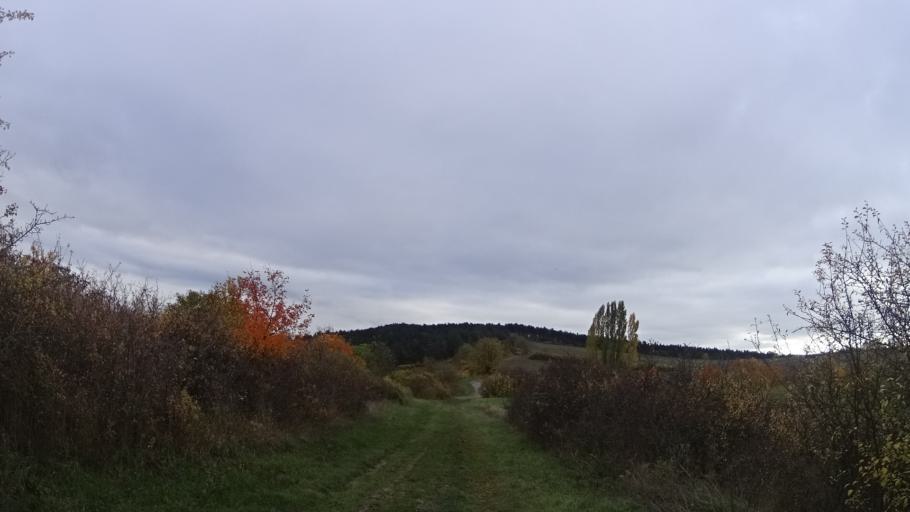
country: DE
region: Thuringia
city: Arnstadt
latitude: 50.8408
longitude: 10.8977
